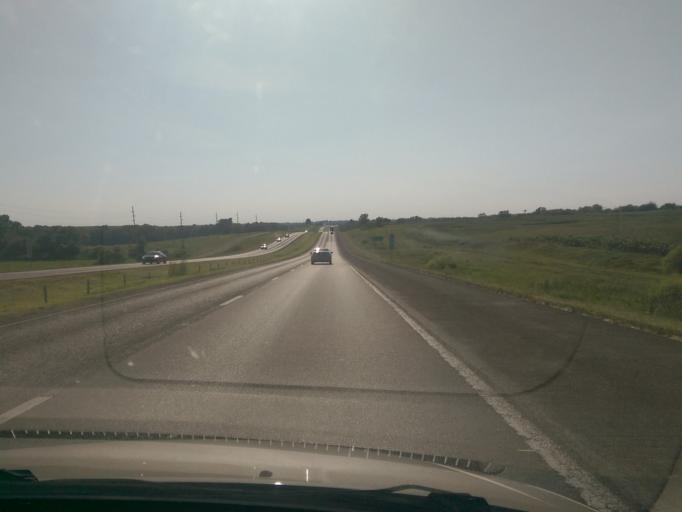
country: US
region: Missouri
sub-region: Lafayette County
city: Higginsville
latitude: 38.9927
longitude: -93.6889
